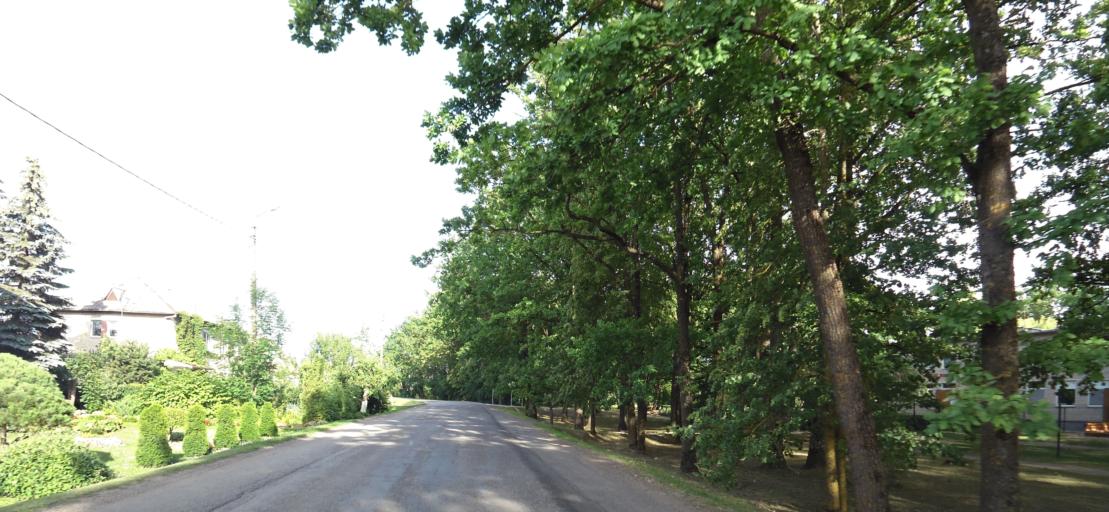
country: LT
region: Panevezys
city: Pasvalys
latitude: 56.1078
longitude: 24.4945
